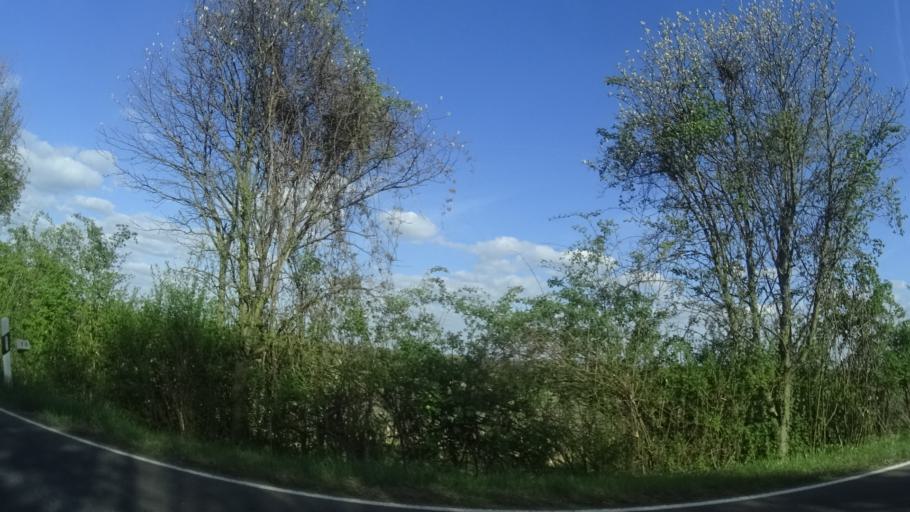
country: DE
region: Rheinland-Pfalz
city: Dienheim
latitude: 49.8306
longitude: 8.3487
